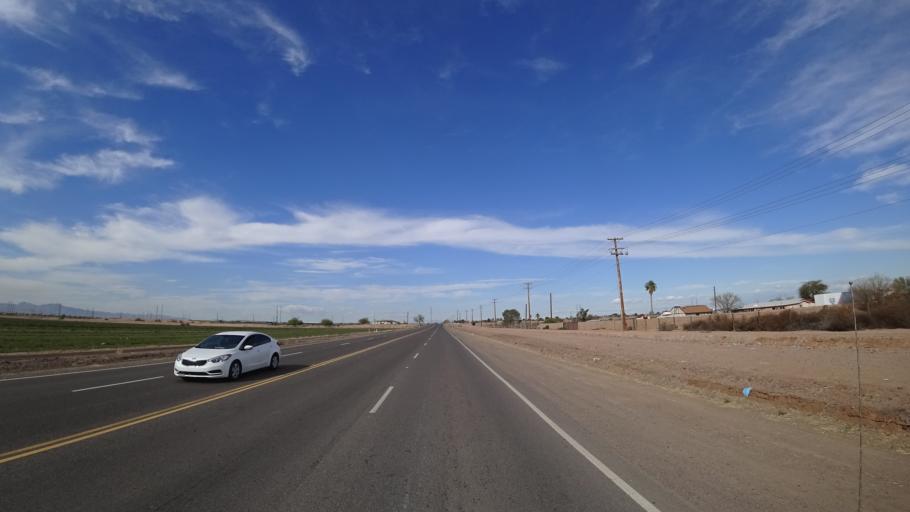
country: US
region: Arizona
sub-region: Maricopa County
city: Avondale
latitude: 33.4066
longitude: -112.3062
